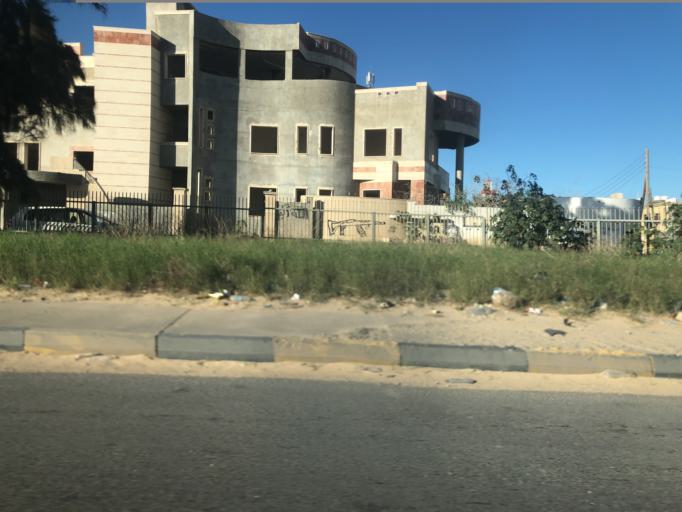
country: LY
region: Tripoli
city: Tripoli
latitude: 32.8698
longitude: 13.2621
